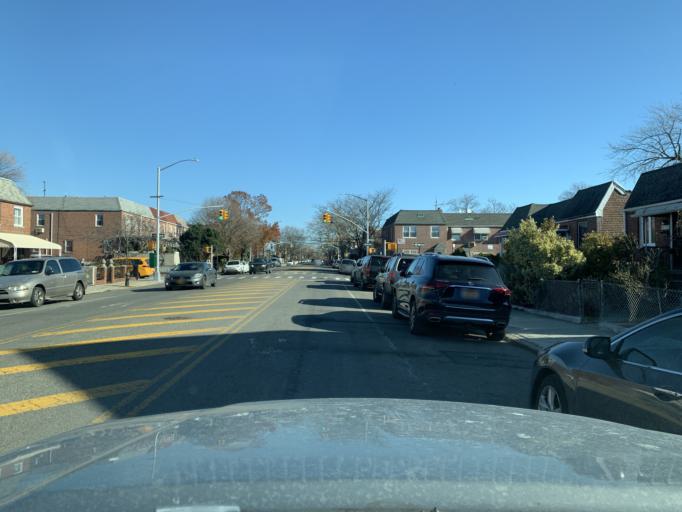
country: US
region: New York
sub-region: Queens County
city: Long Island City
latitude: 40.7610
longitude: -73.8878
